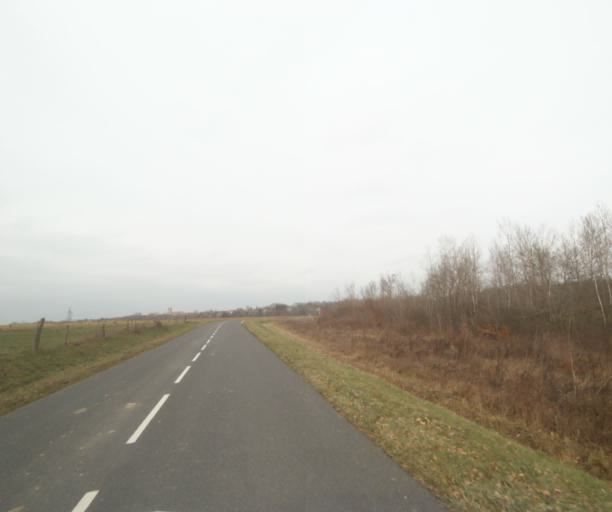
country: FR
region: Champagne-Ardenne
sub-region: Departement de la Marne
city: Pargny-sur-Saulx
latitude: 48.7425
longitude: 4.8608
